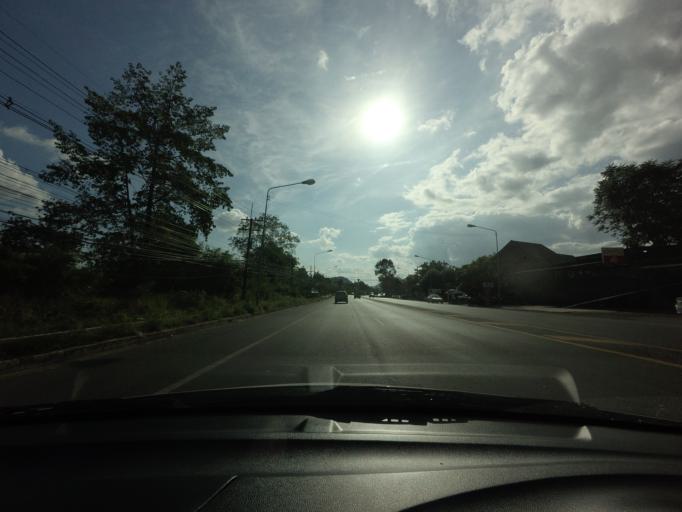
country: TH
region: Nakhon Nayok
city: Nakhon Nayok
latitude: 14.3185
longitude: 101.3029
